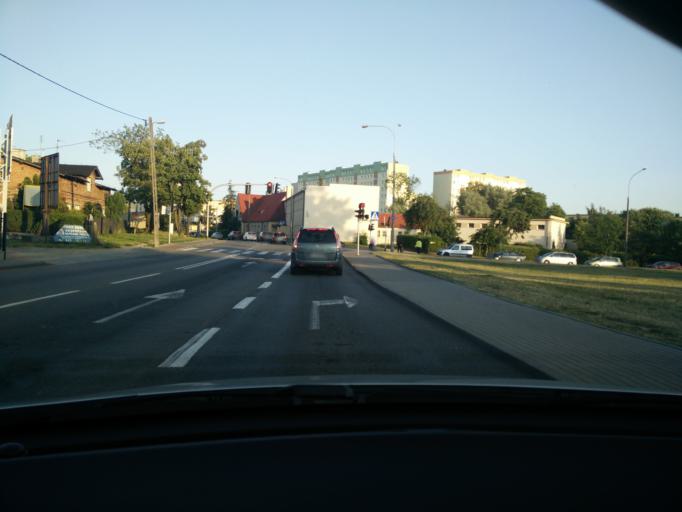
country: PL
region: Pomeranian Voivodeship
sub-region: Gdynia
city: Pogorze
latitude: 54.5599
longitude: 18.5106
